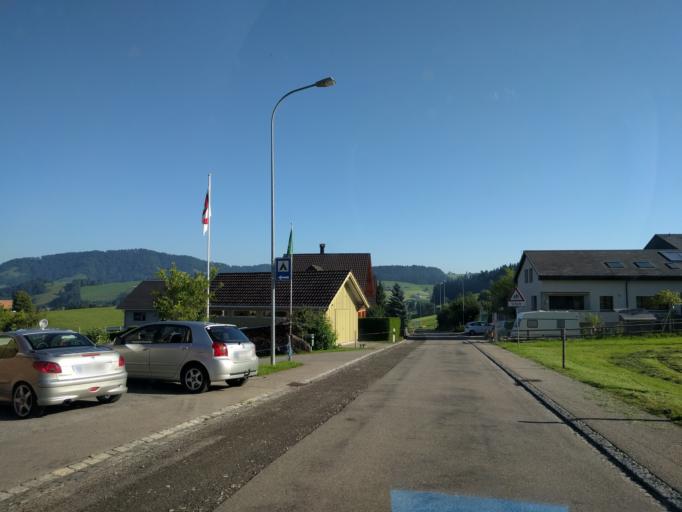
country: CH
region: Saint Gallen
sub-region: Wahlkreis Toggenburg
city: Sankt Peterzell
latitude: 47.3064
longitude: 9.1953
